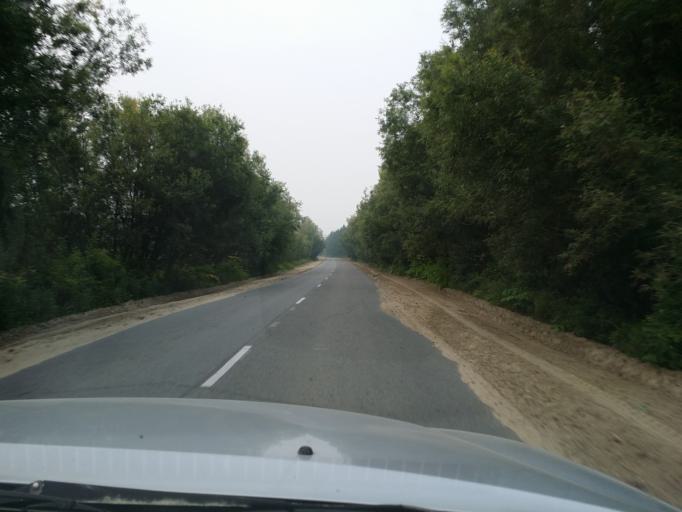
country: RU
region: Khanty-Mansiyskiy Avtonomnyy Okrug
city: Megion
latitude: 61.0032
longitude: 76.3073
